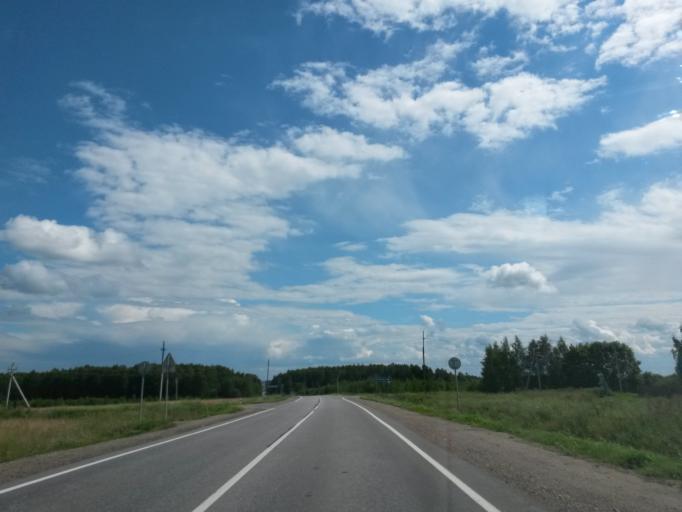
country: RU
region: Jaroslavl
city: Gavrilov-Yam
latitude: 57.2698
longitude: 39.9640
